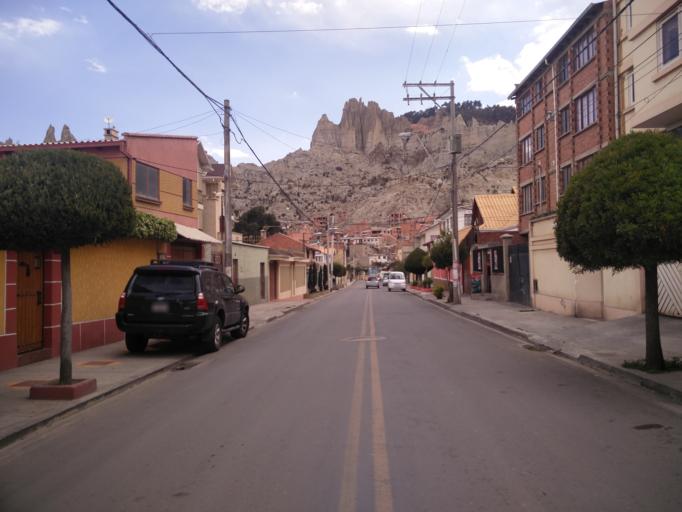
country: BO
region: La Paz
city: La Paz
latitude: -16.5193
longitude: -68.1307
